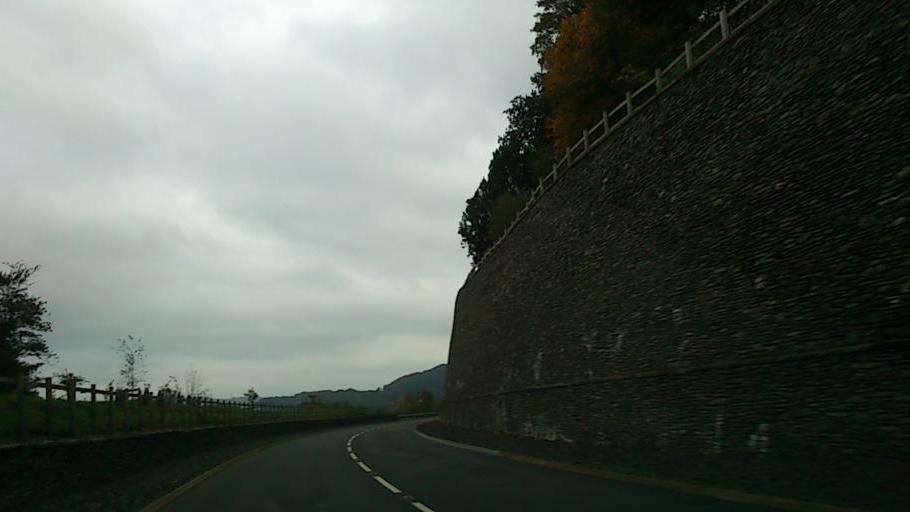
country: GB
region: Wales
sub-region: Sir Powys
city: Machynlleth
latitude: 52.5520
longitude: -3.9323
